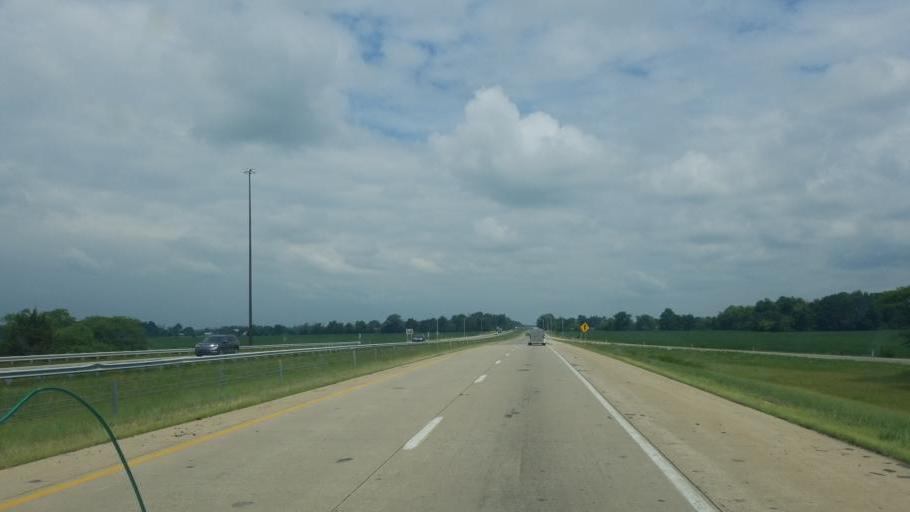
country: US
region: Indiana
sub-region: Madison County
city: Alexandria
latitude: 40.2770
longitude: -85.5578
